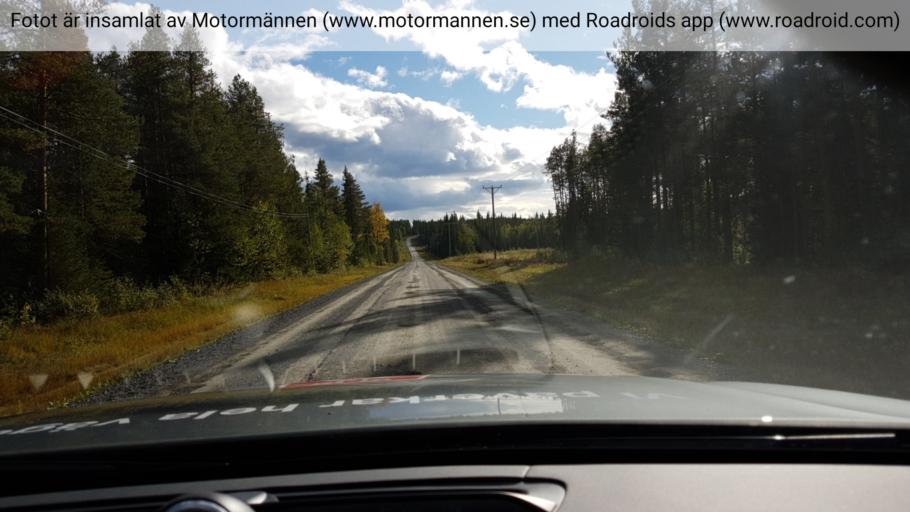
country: SE
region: Jaemtland
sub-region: Are Kommun
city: Jarpen
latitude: 63.2954
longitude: 13.6461
